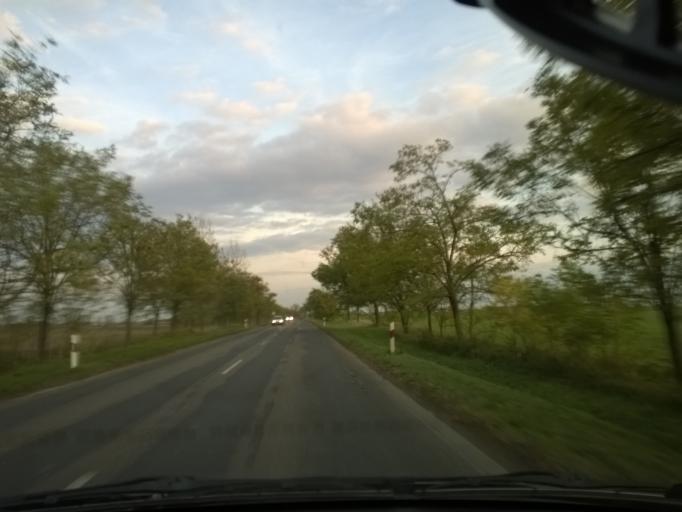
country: HU
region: Bacs-Kiskun
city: Kiskunfelegyhaza
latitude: 46.7016
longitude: 19.9064
